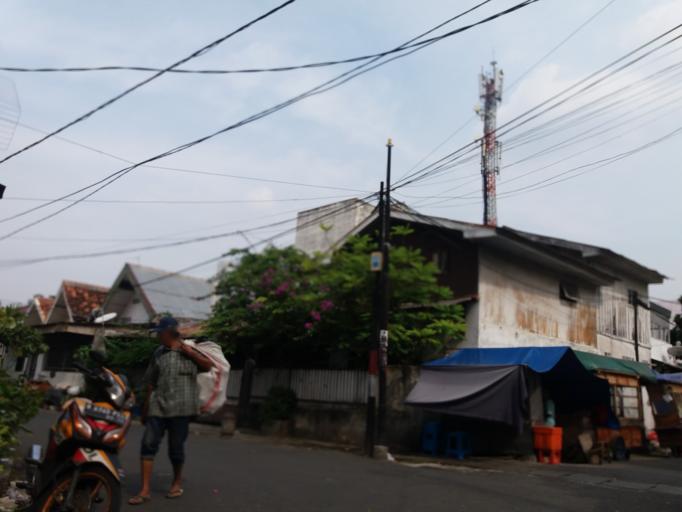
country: ID
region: Jakarta Raya
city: Jakarta
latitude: -6.1843
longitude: 106.8259
